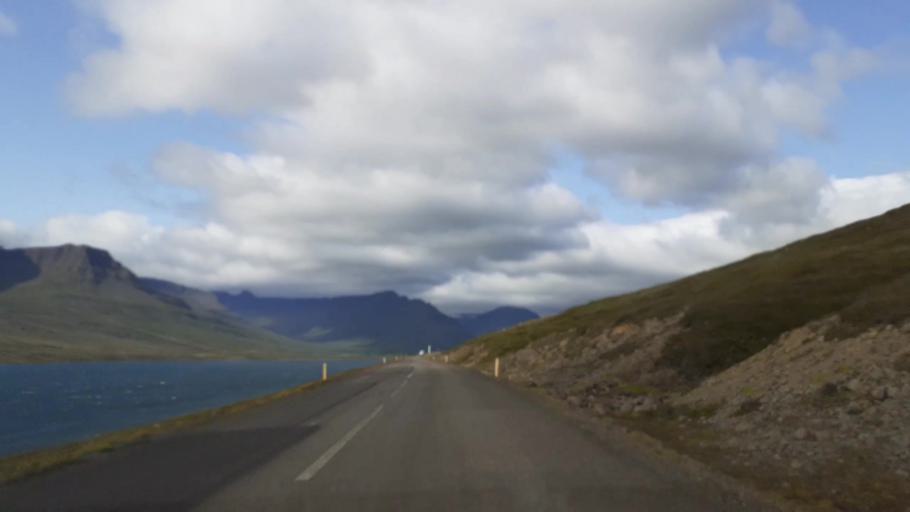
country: IS
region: East
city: Eskifjoerdur
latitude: 64.9218
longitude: -13.9657
